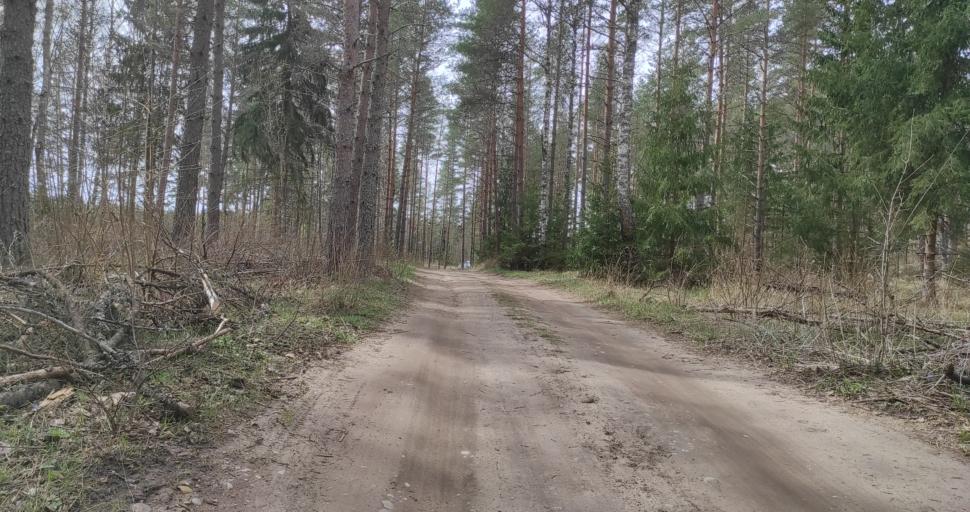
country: LV
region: Talsu Rajons
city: Stende
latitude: 57.0828
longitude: 22.3792
